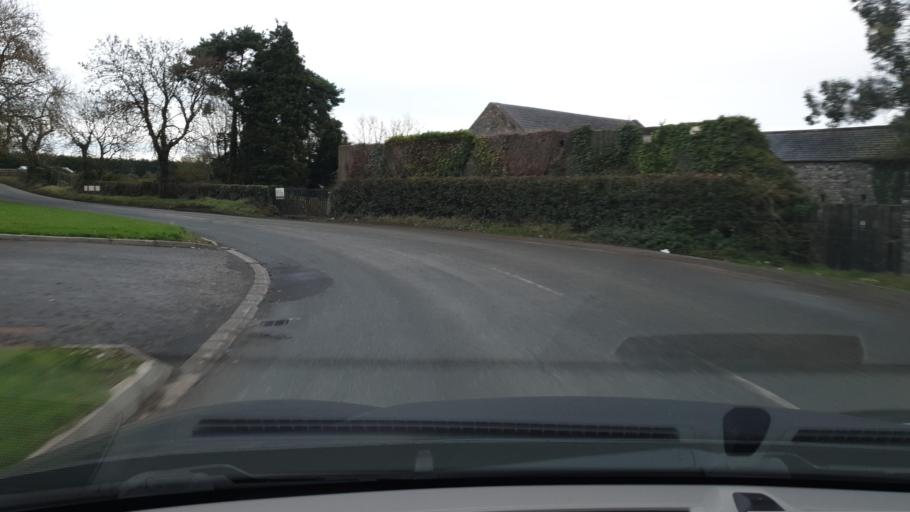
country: IE
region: Leinster
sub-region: An Mhi
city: Ashbourne
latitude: 53.5257
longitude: -6.4104
